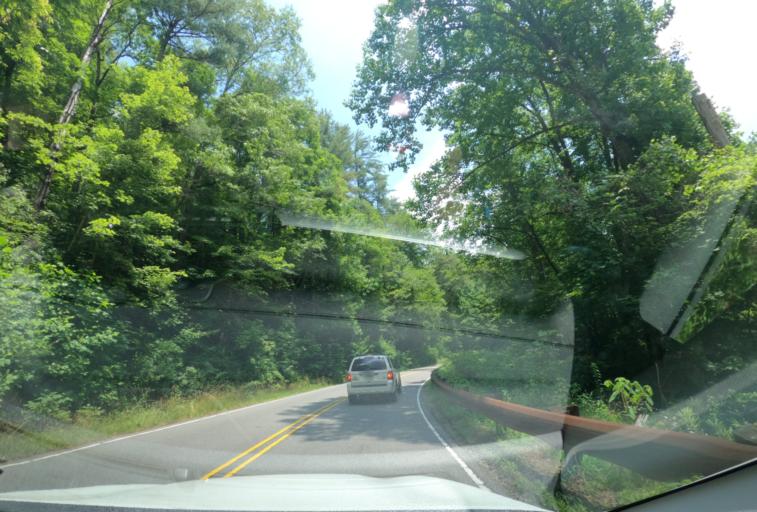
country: US
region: North Carolina
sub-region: Macon County
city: Franklin
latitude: 35.0724
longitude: -83.2324
